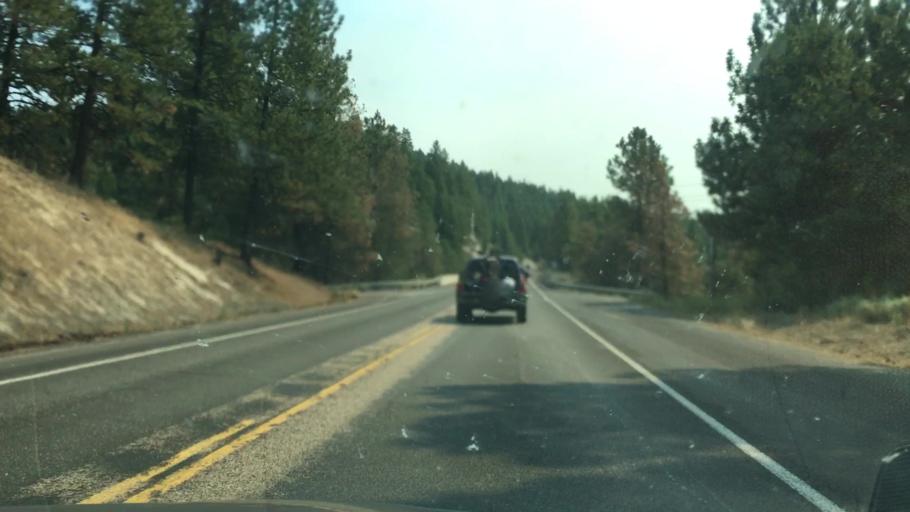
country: US
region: Idaho
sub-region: Valley County
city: Cascade
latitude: 44.5898
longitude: -116.0394
